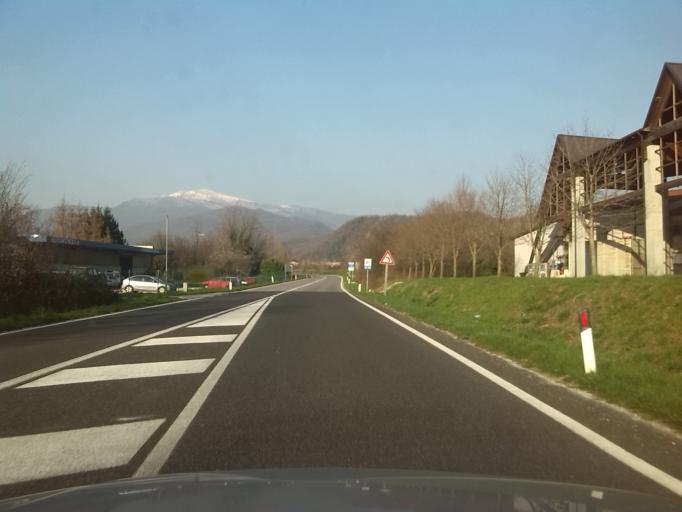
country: IT
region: Friuli Venezia Giulia
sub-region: Provincia di Udine
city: San Pietro al Natisone
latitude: 46.1157
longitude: 13.4804
